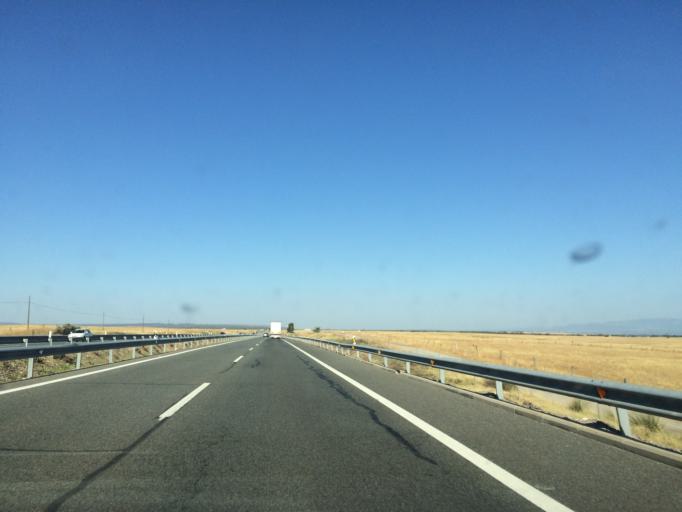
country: ES
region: Extremadura
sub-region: Provincia de Caceres
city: Berrocalejo
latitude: 39.8926
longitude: -5.3784
